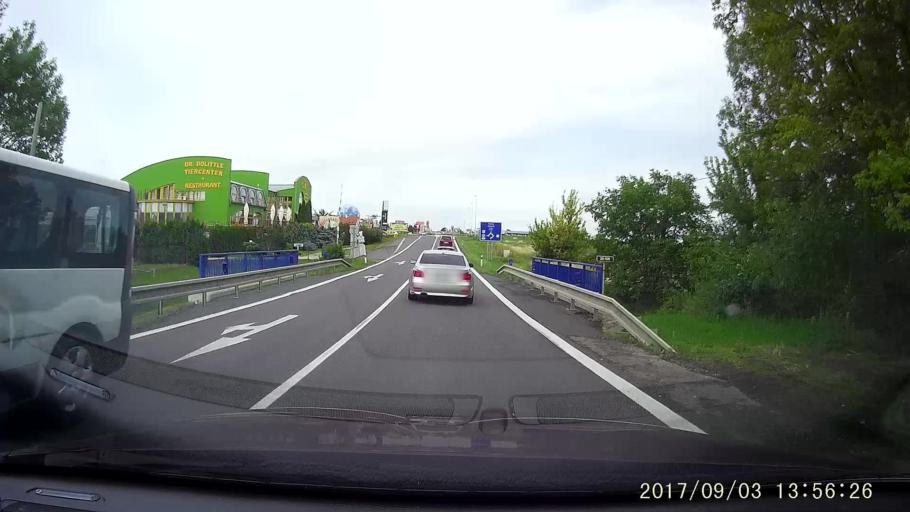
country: CZ
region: South Moravian
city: Vrbovec
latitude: 48.7608
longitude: 16.0636
